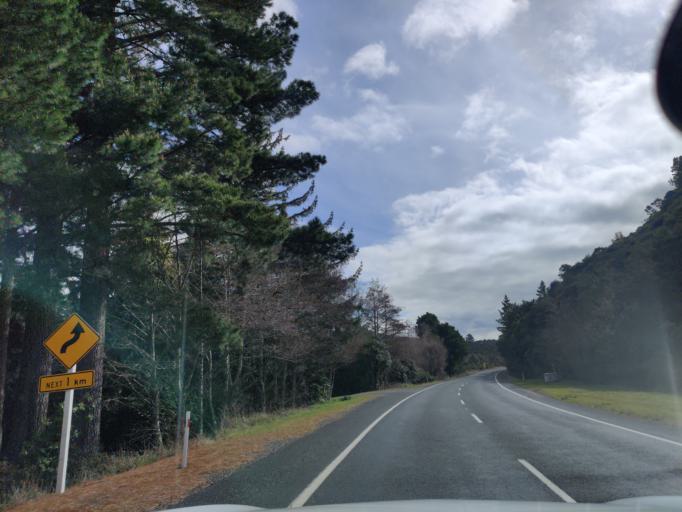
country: NZ
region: Waikato
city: Turangi
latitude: -38.9778
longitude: 175.7725
